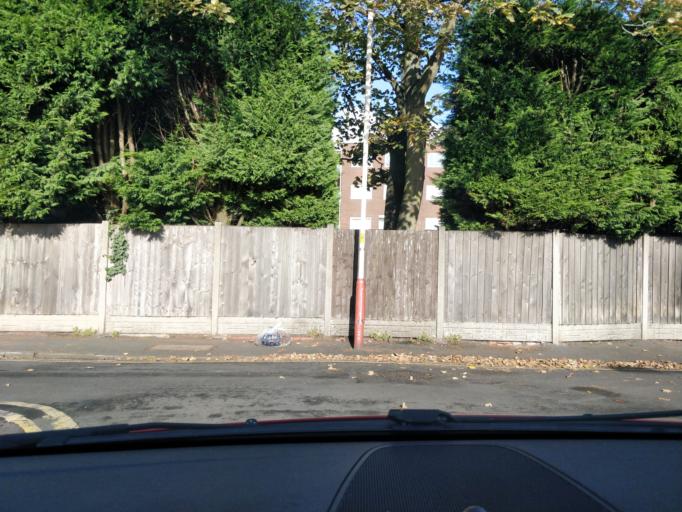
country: GB
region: England
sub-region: Sefton
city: Southport
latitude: 53.6422
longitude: -3.0133
